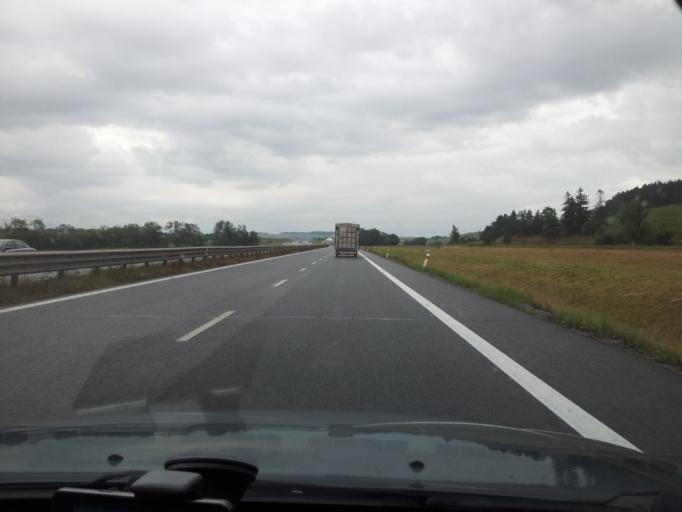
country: SK
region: Presovsky
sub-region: Okres Poprad
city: Poprad
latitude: 49.0883
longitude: 20.3360
